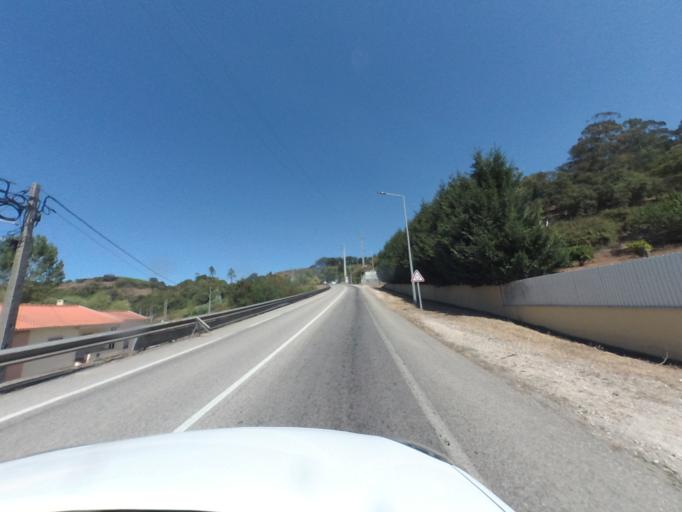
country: PT
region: Leiria
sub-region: Alcobaca
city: Alcobaca
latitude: 39.5378
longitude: -8.9888
